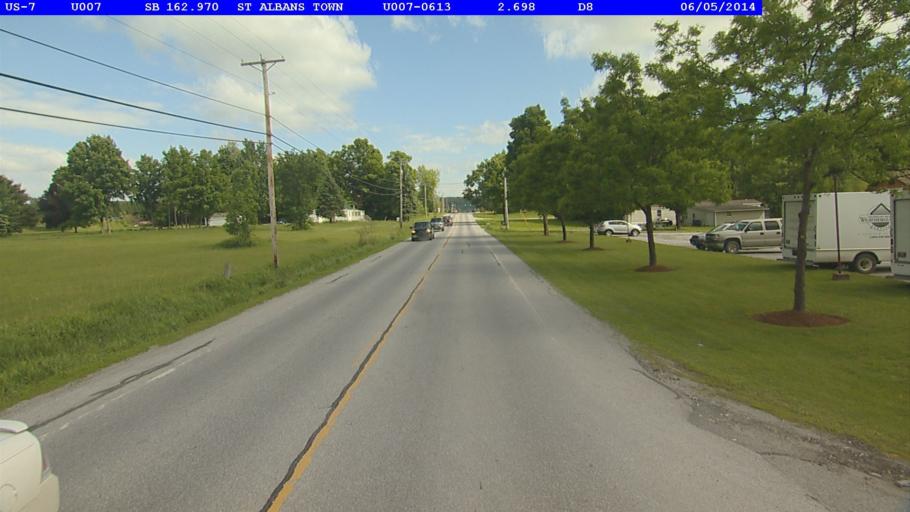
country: US
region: Vermont
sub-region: Franklin County
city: Saint Albans
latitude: 44.8464
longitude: -73.0871
